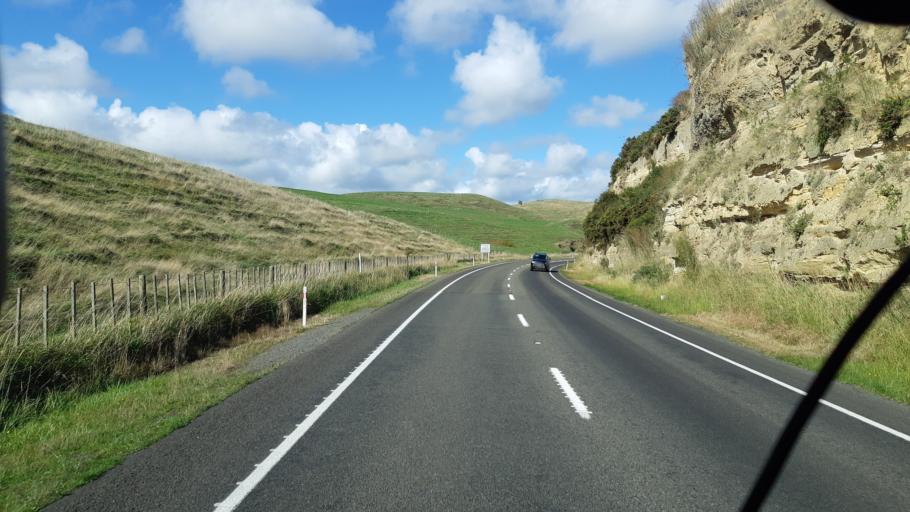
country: NZ
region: Manawatu-Wanganui
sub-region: Wanganui District
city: Wanganui
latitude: -40.0180
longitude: 175.1760
